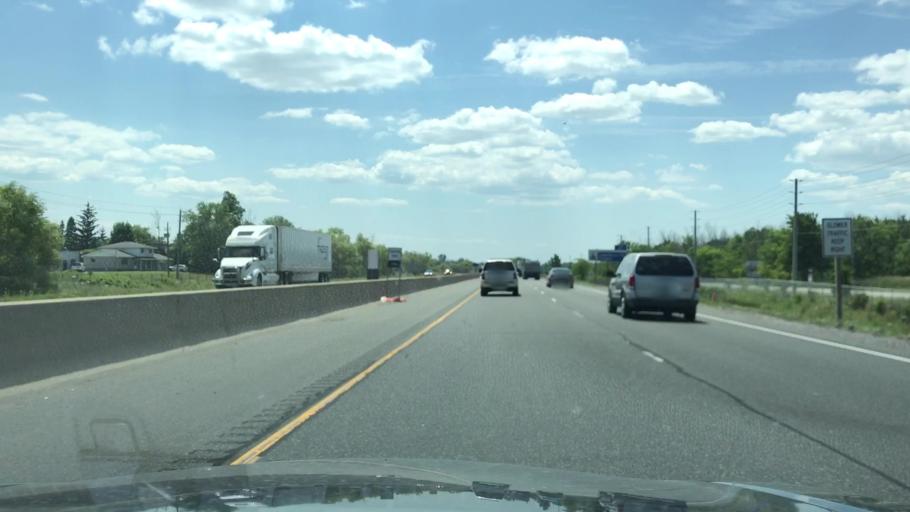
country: CA
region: Ontario
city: Niagara Falls
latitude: 43.0613
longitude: -79.1226
